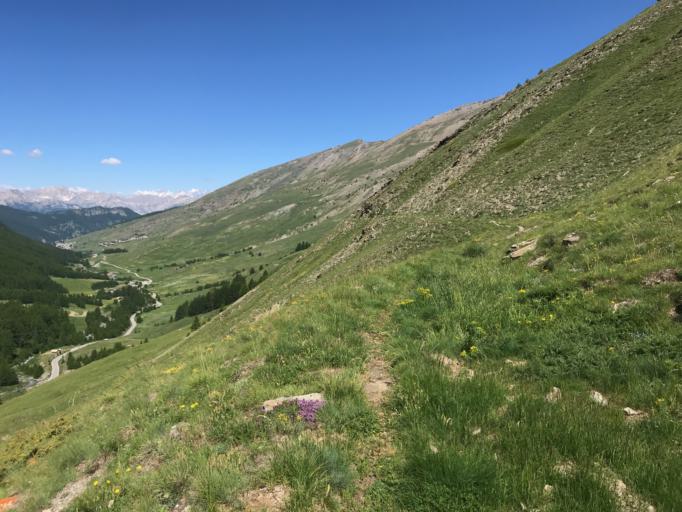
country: IT
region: Piedmont
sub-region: Provincia di Cuneo
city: Pontechianale
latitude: 44.7138
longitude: 6.9226
